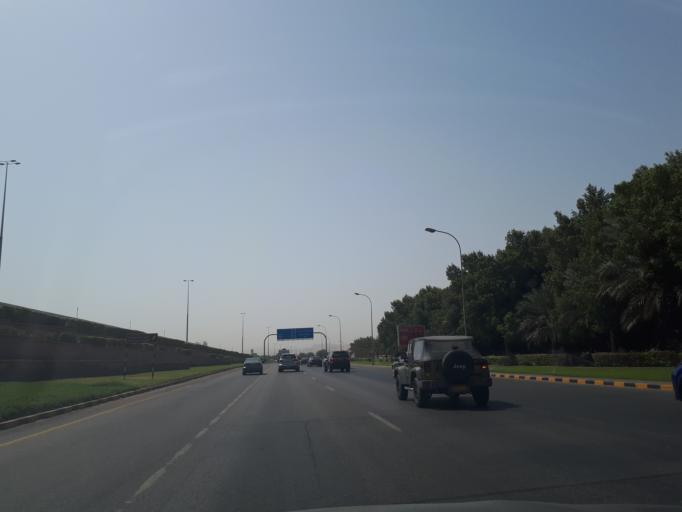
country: OM
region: Muhafazat Masqat
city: As Sib al Jadidah
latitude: 23.6117
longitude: 58.2454
